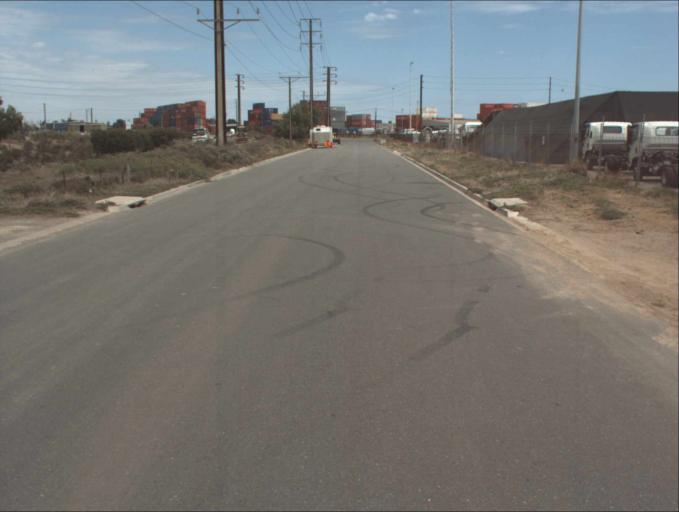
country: AU
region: South Australia
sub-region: Port Adelaide Enfield
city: Birkenhead
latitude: -34.8348
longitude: 138.5195
